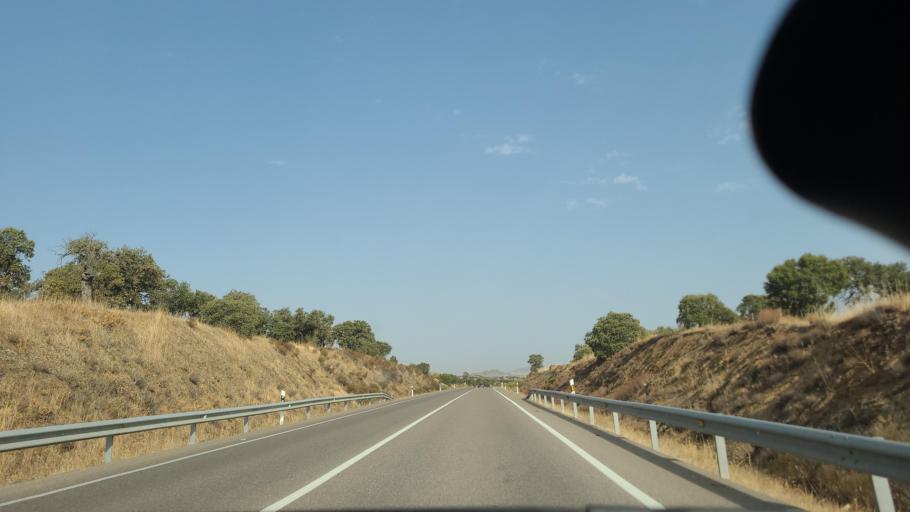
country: ES
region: Andalusia
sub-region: Province of Cordoba
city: Belmez
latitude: 38.2263
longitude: -5.1613
